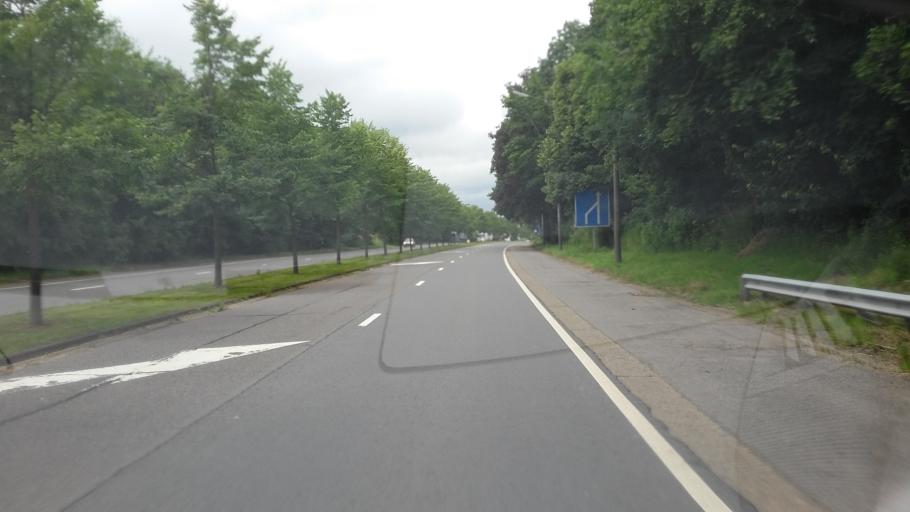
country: BE
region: Wallonia
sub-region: Province du Luxembourg
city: Arlon
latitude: 49.6927
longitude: 5.8133
